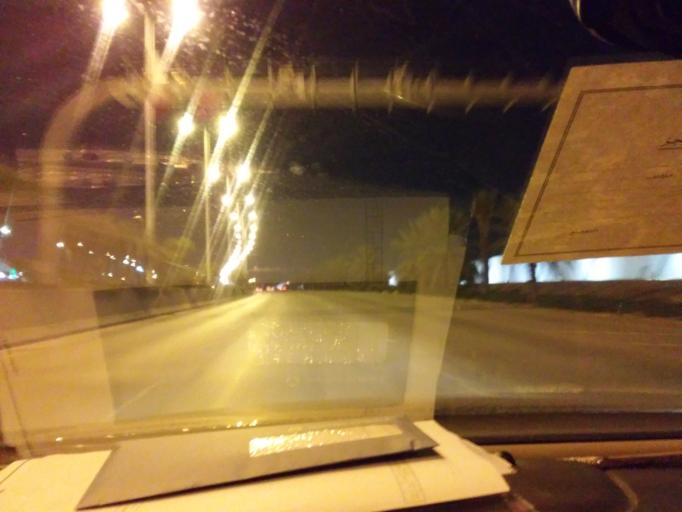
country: SA
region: Ar Riyad
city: Riyadh
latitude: 24.7229
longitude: 46.6977
